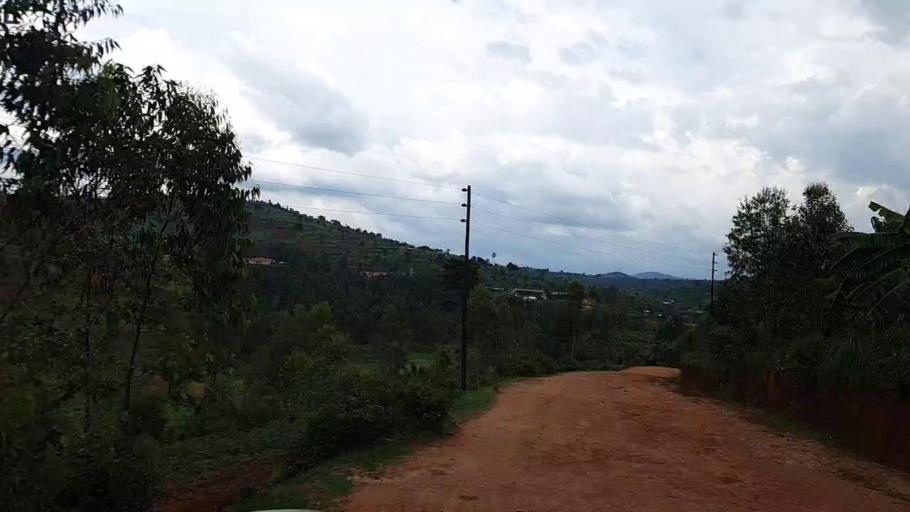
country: RW
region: Southern Province
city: Gikongoro
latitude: -2.4161
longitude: 29.6573
